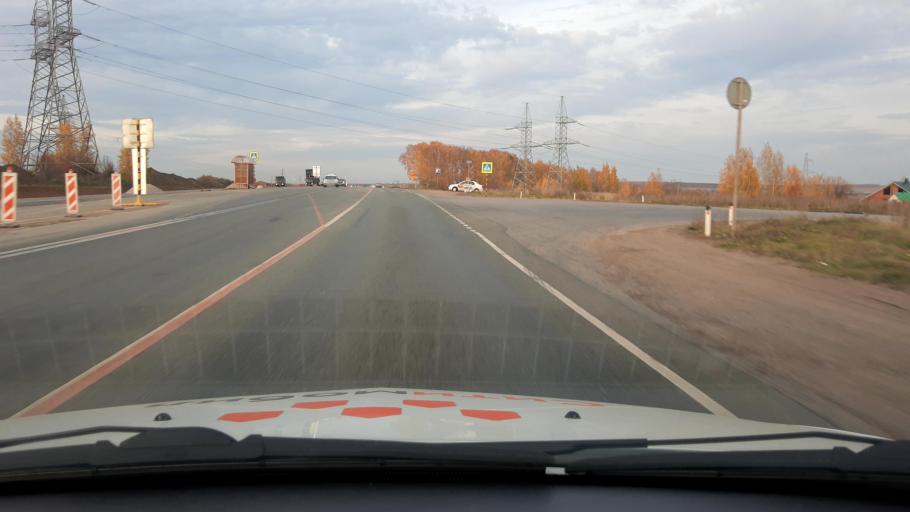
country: RU
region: Bashkortostan
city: Kabakovo
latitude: 54.6785
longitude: 56.1894
